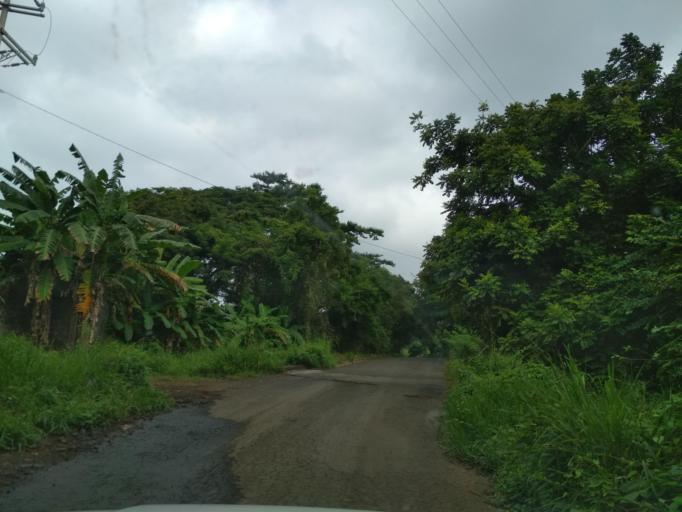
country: MX
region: Veracruz
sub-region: San Andres Tuxtla
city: Matacapan
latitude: 18.4456
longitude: -95.1808
